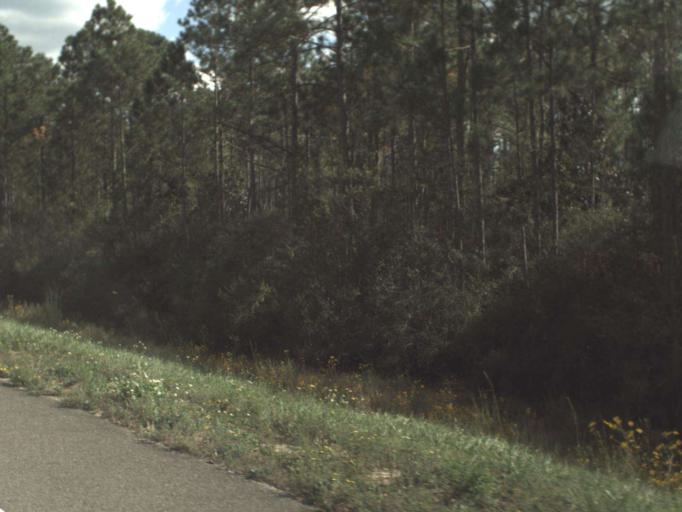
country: US
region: Florida
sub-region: Bay County
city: Laguna Beach
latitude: 30.4570
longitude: -85.9163
